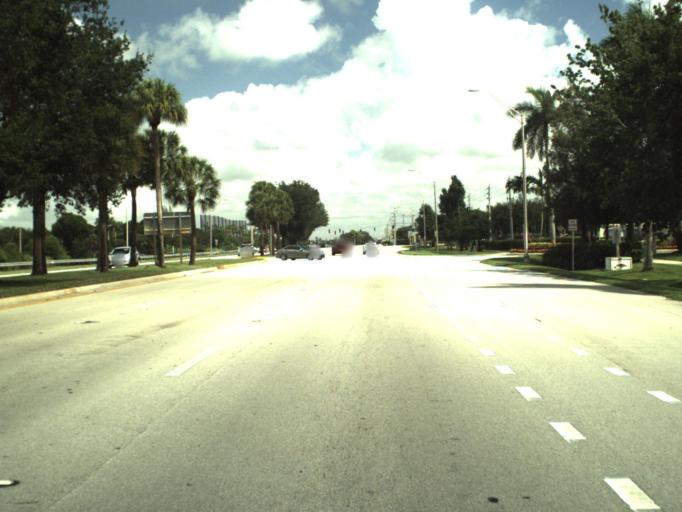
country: US
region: Florida
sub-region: Broward County
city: Sunshine Ranches
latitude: 26.0120
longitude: -80.3119
